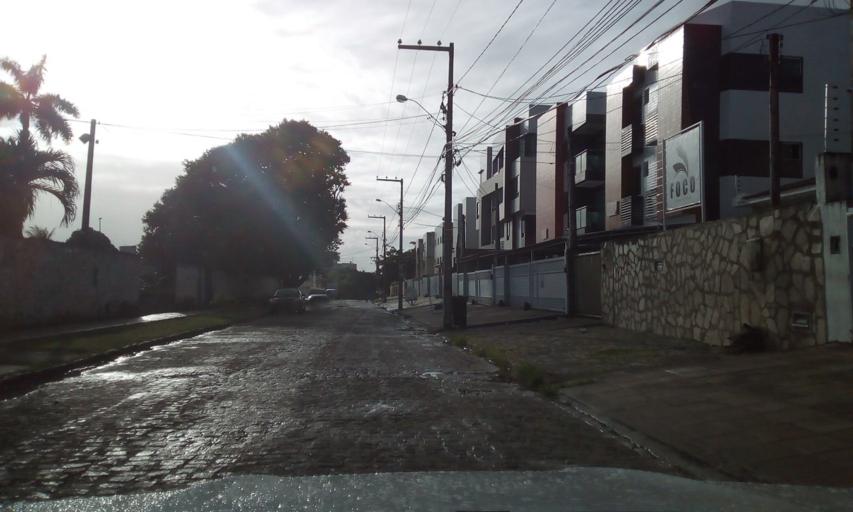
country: BR
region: Paraiba
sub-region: Joao Pessoa
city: Joao Pessoa
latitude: -7.1487
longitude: -34.8353
